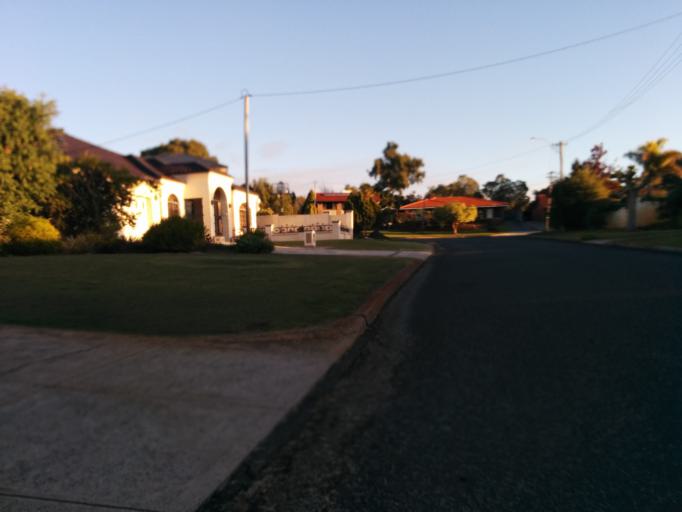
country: AU
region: Western Australia
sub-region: Canning
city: Rossmoyne
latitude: -32.0504
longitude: 115.8609
